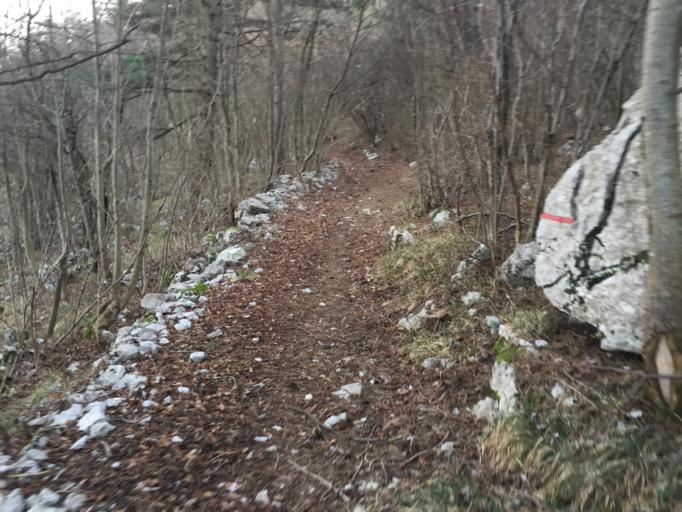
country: SI
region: Kanal
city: Kanal
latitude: 46.0387
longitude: 13.6807
